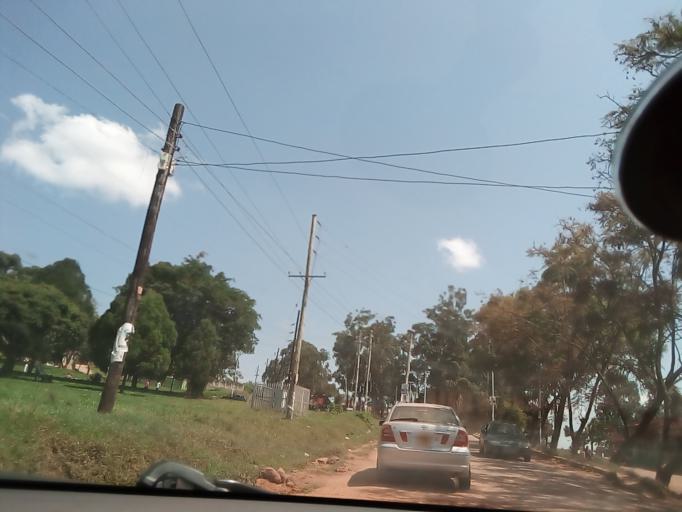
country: UG
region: Central Region
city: Masaka
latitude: -0.3308
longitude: 31.7387
